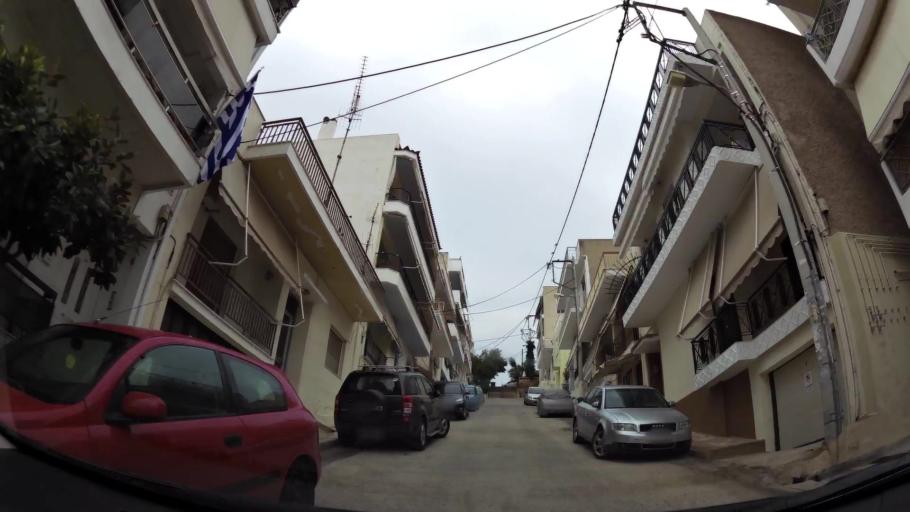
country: GR
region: Attica
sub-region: Nomos Piraios
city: Korydallos
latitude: 37.9841
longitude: 23.6380
